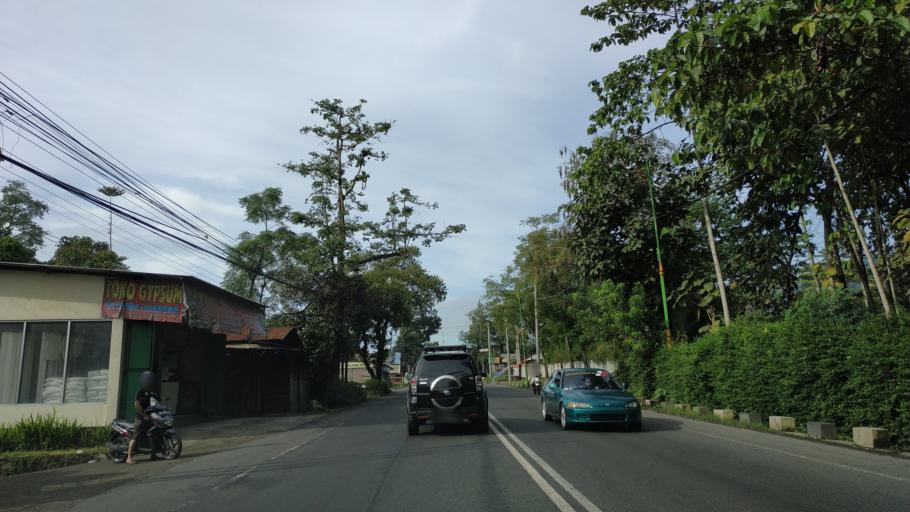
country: ID
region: Central Java
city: Salatiga
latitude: -7.3812
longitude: 110.5151
